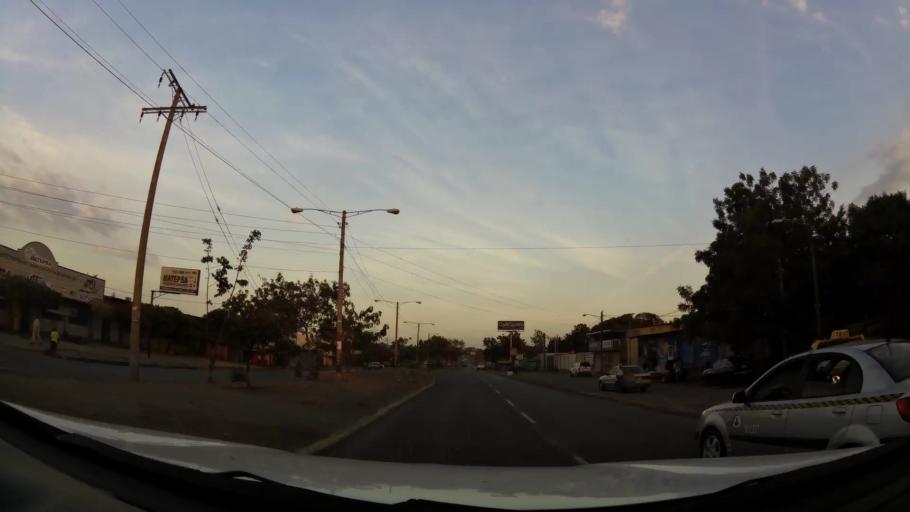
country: NI
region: Managua
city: Managua
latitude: 12.1383
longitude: -86.2041
